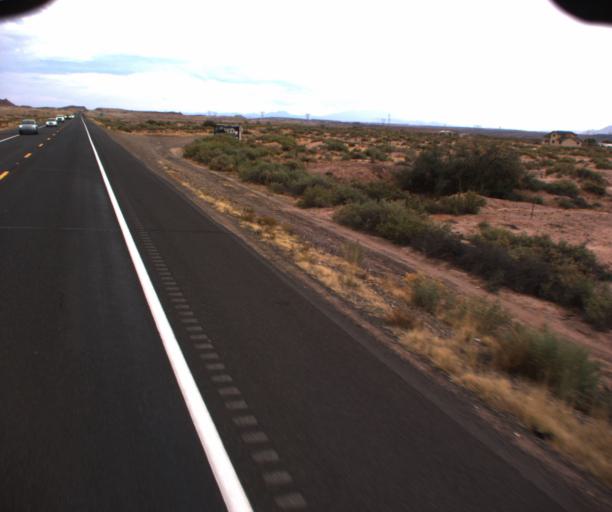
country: US
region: Arizona
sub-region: Coconino County
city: Tuba City
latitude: 36.0152
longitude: -111.3958
